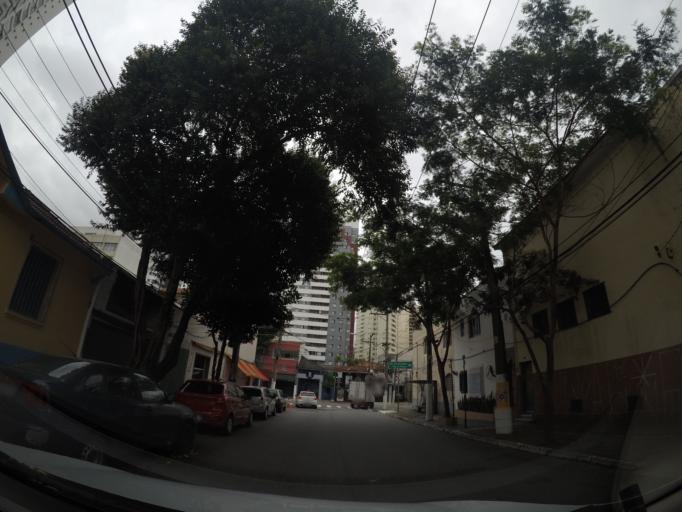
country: BR
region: Sao Paulo
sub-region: Sao Paulo
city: Sao Paulo
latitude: -23.5571
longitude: -46.6030
